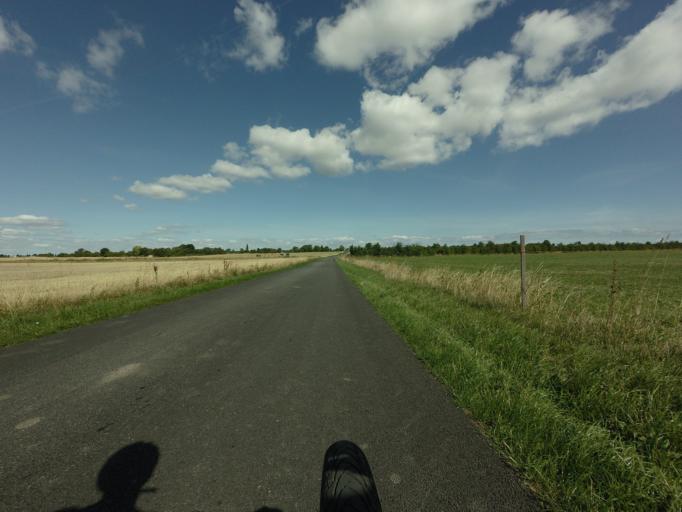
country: DK
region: Zealand
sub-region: Vordingborg Kommune
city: Stege
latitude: 54.9686
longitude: 12.3589
